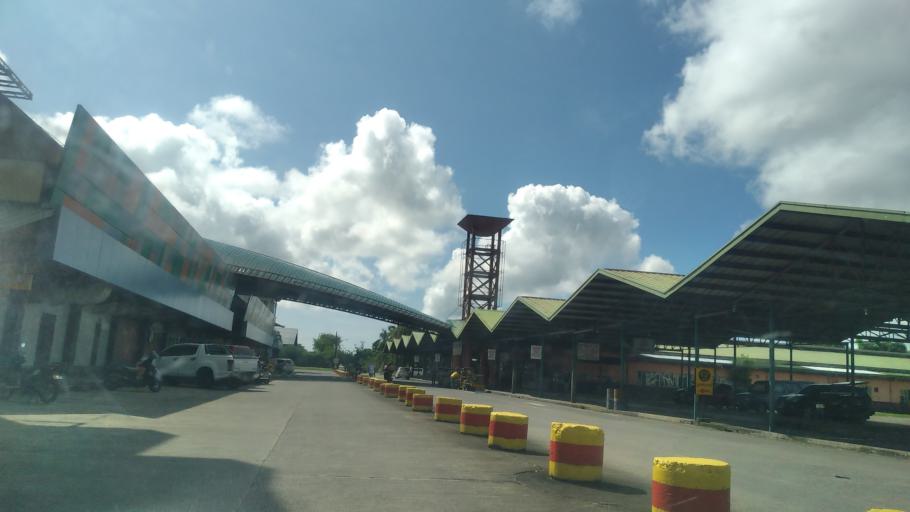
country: PH
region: Calabarzon
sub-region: Province of Quezon
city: Lucena
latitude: 13.9588
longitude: 121.6178
